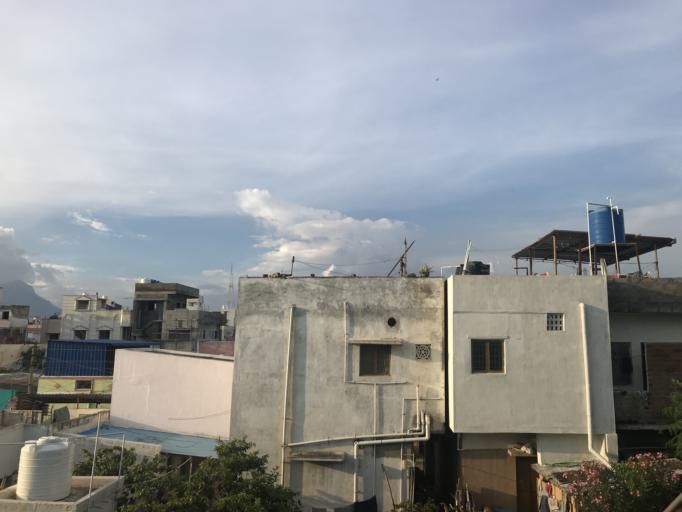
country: IN
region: Tamil Nadu
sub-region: Coimbatore
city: Coimbatore
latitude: 11.0315
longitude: 76.9587
